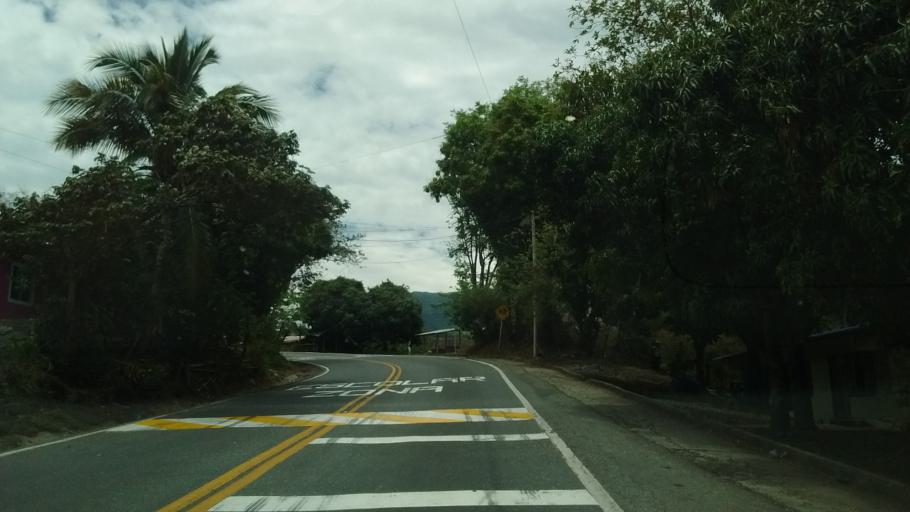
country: CO
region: Cauca
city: La Sierra
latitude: 2.2144
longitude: -76.7964
